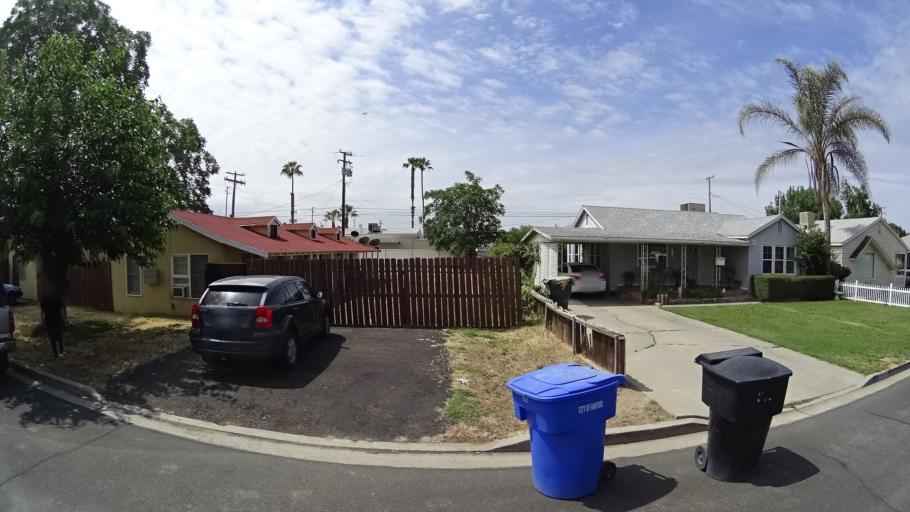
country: US
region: California
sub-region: Kings County
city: Hanford
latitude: 36.3340
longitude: -119.6376
